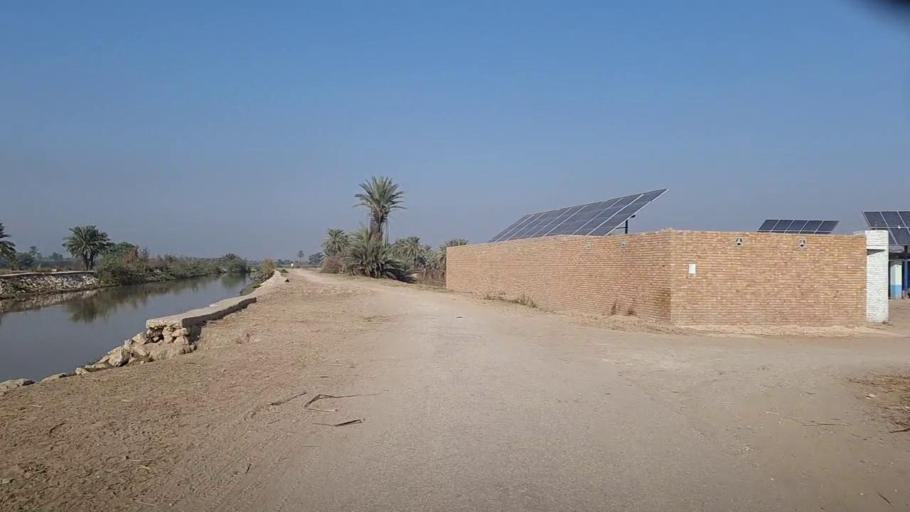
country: PK
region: Sindh
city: Ranipur
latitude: 27.2436
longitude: 68.5528
